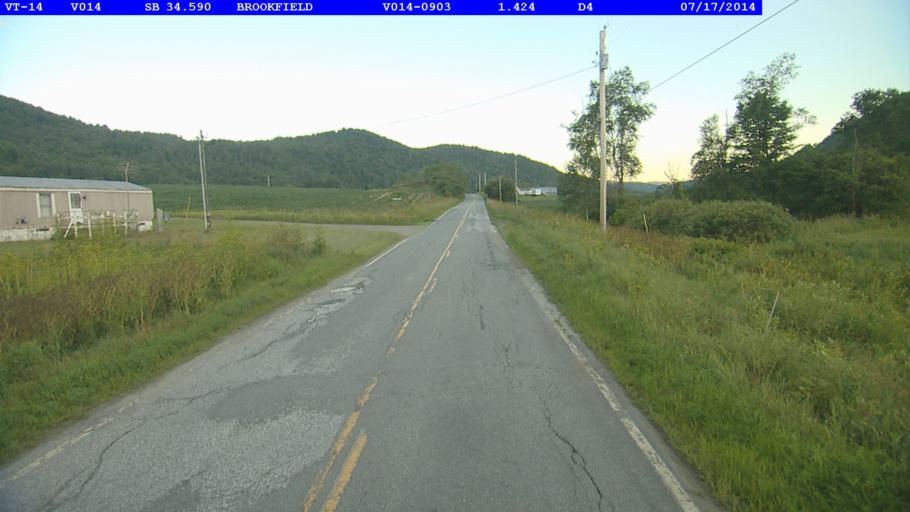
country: US
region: Vermont
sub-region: Orange County
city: Chelsea
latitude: 43.9989
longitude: -72.5599
